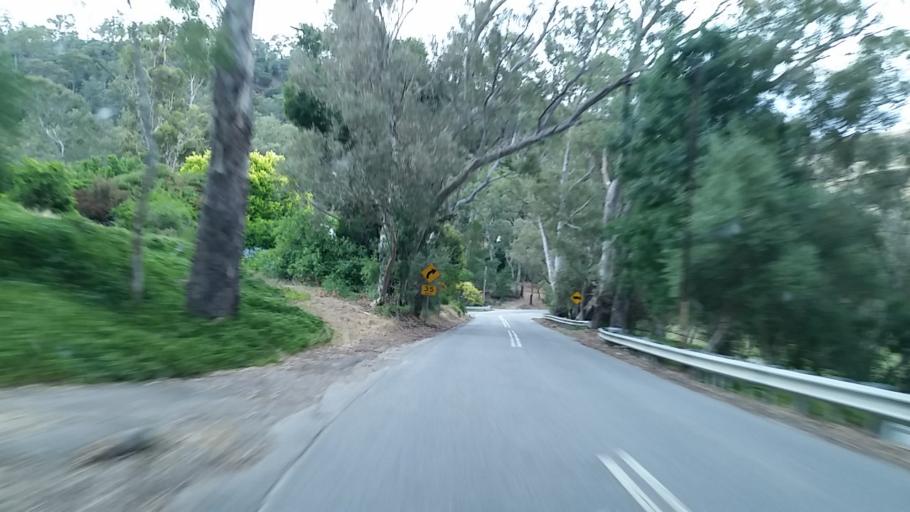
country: AU
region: South Australia
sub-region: Campbelltown
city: Athelstone
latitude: -34.8675
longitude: 138.7567
